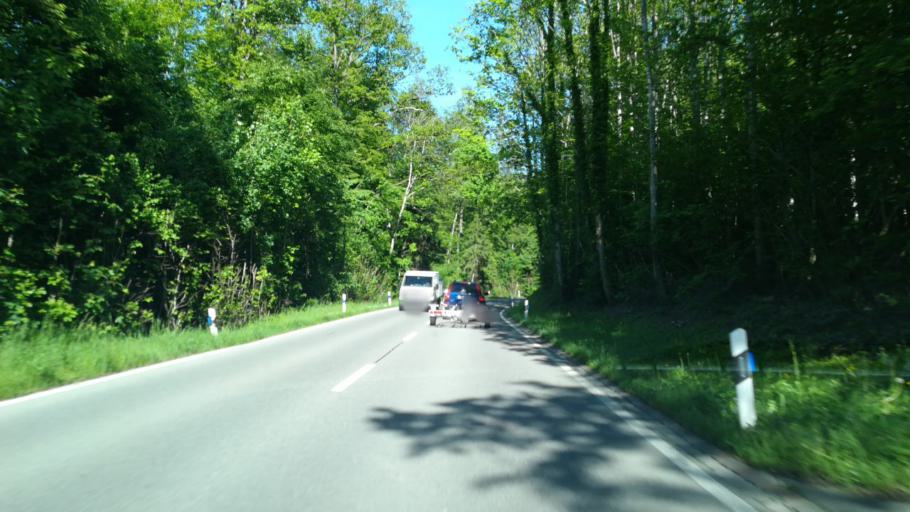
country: CH
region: Thurgau
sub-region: Frauenfeld District
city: Wagenhausen
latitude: 47.6586
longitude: 8.7999
